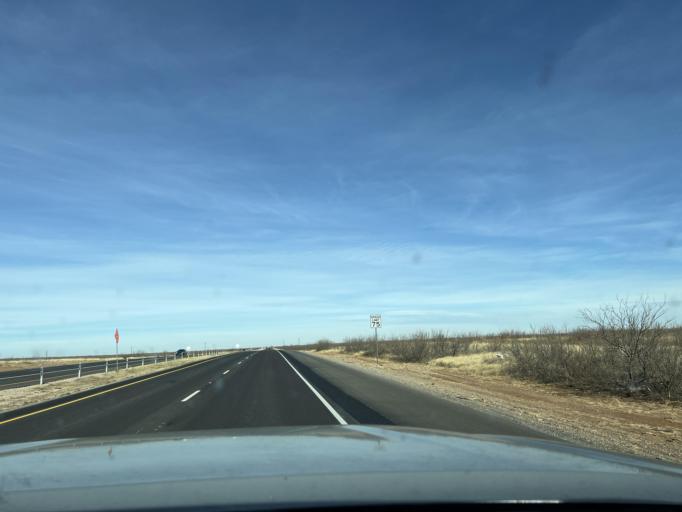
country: US
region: Texas
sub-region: Ector County
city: Gardendale
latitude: 32.0898
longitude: -102.4515
